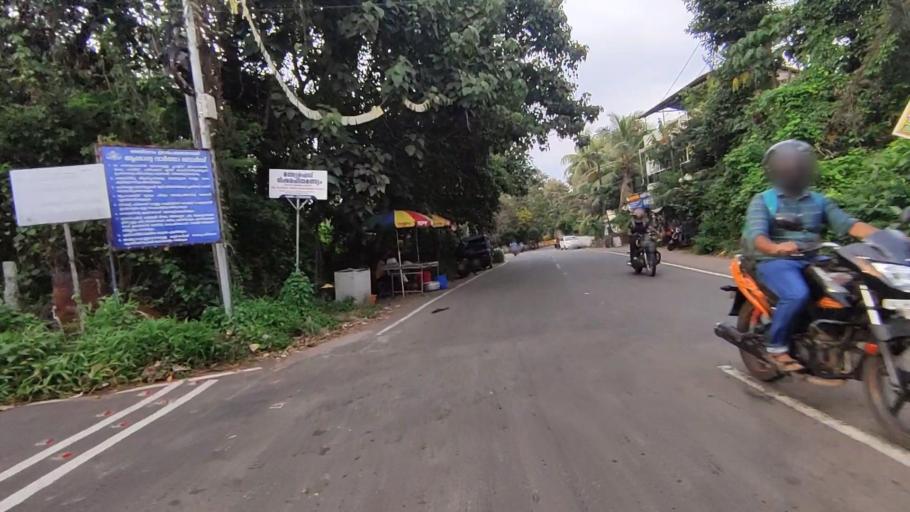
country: IN
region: Kerala
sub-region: Kottayam
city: Kottayam
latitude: 9.6196
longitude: 76.5105
